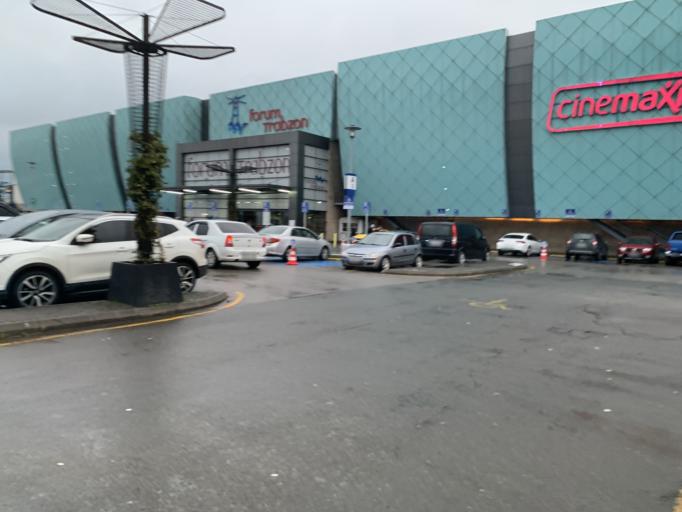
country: TR
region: Trabzon
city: Trabzon
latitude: 40.9995
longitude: 39.7593
